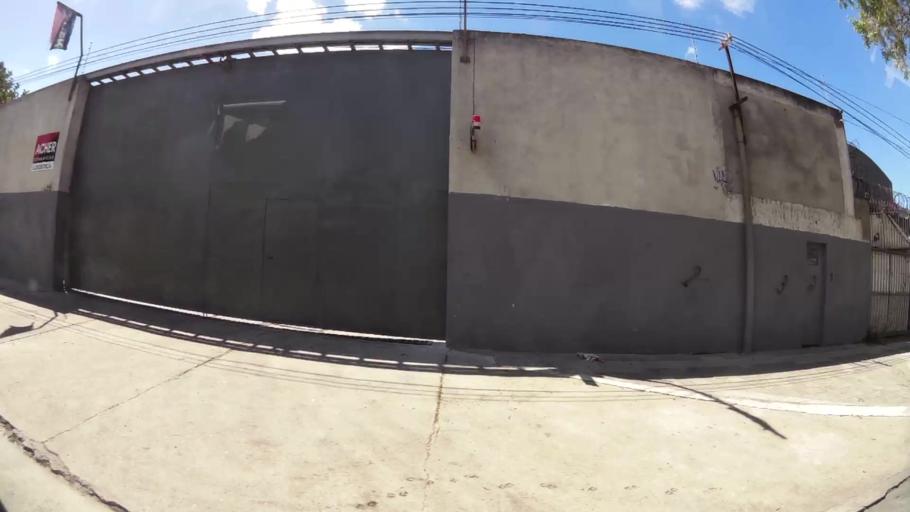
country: UY
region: Montevideo
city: Montevideo
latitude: -34.8553
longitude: -56.1341
